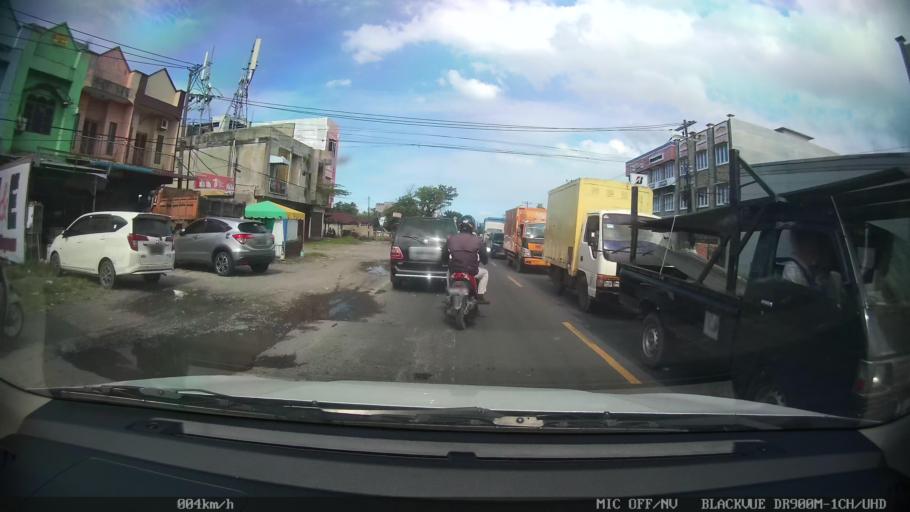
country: ID
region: North Sumatra
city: Medan
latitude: 3.6154
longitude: 98.6454
